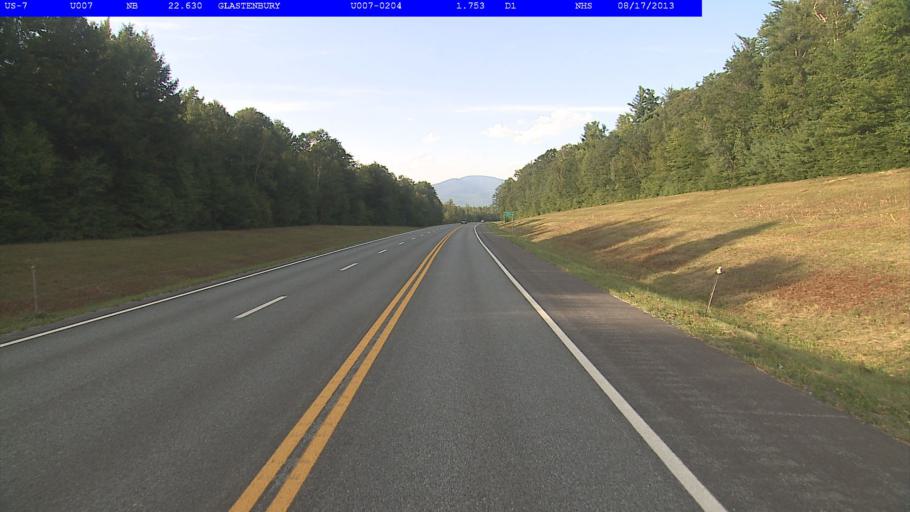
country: US
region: Vermont
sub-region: Bennington County
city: Arlington
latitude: 43.0253
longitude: -73.1400
